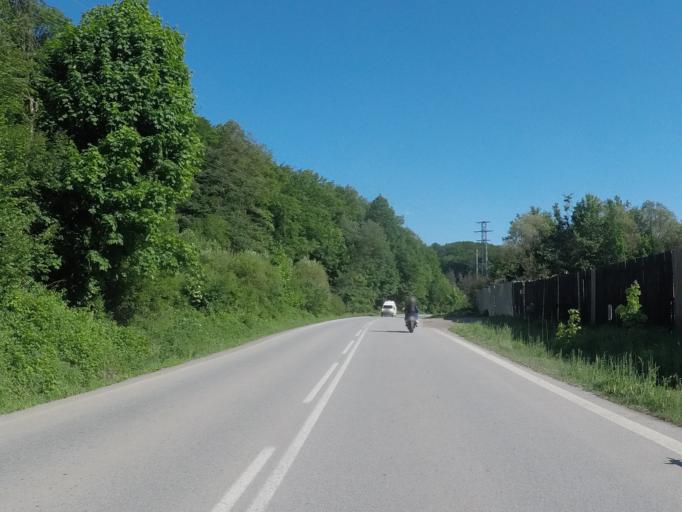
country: SK
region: Kosicky
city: Dobsina
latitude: 48.8137
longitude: 20.3857
